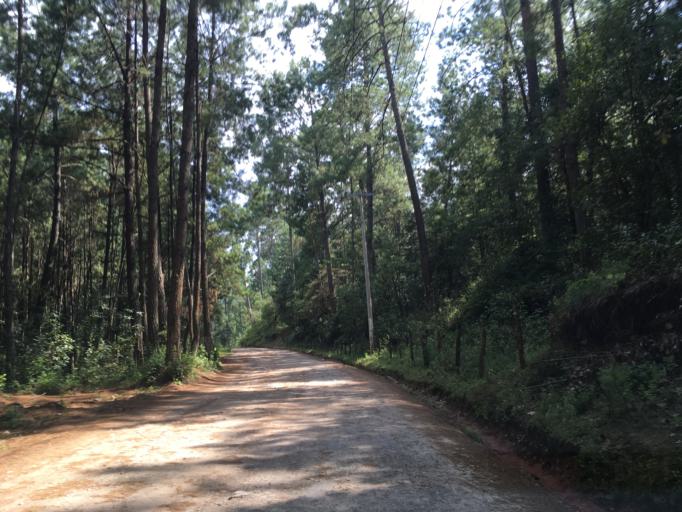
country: MX
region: Michoacan
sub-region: Morelia
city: Morelos
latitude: 19.5495
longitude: -101.1984
